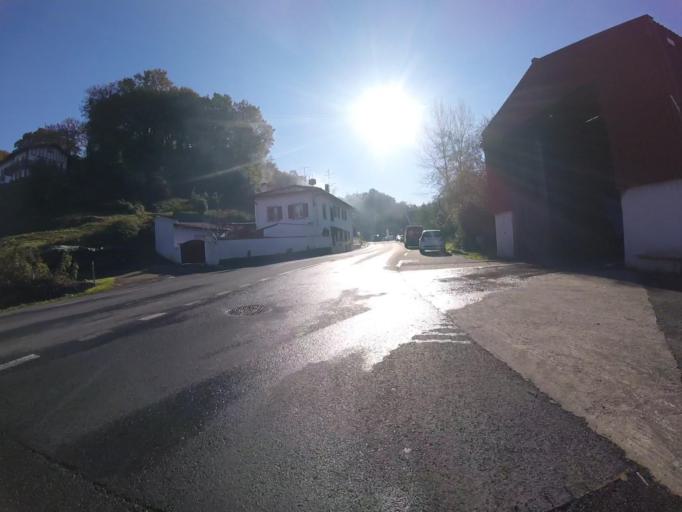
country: ES
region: Basque Country
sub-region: Provincia de Guipuzcoa
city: Irun
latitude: 43.3391
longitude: -1.7511
